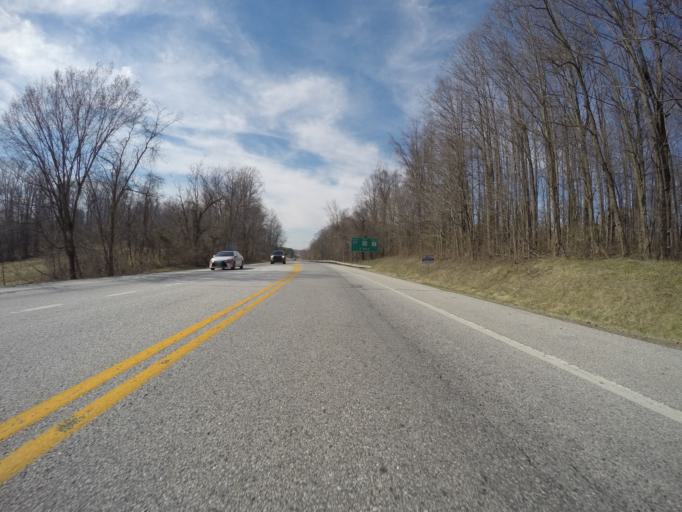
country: US
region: Maryland
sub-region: Anne Arundel County
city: Crownsville
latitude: 39.0413
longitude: -76.6065
